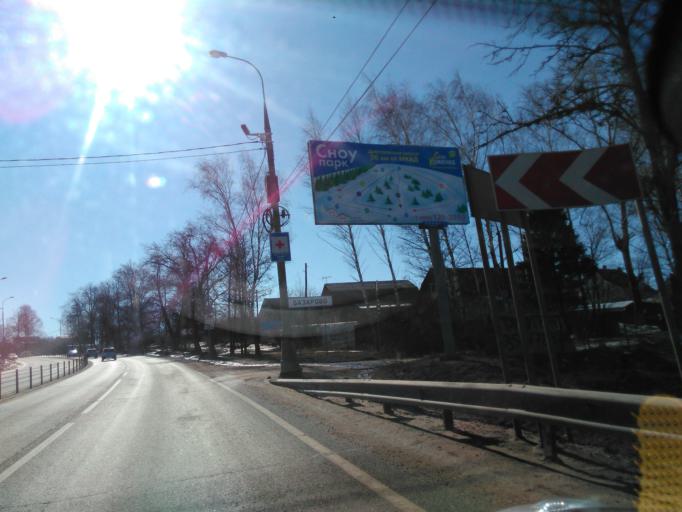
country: RU
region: Moskovskaya
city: Yermolino
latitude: 56.1588
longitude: 37.4889
